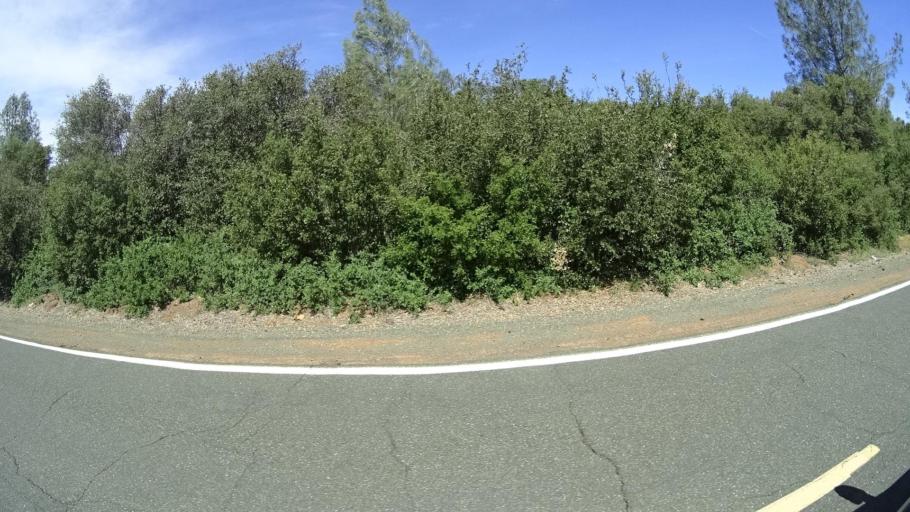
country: US
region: California
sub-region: Lake County
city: Clearlake
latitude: 38.9264
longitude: -122.6592
